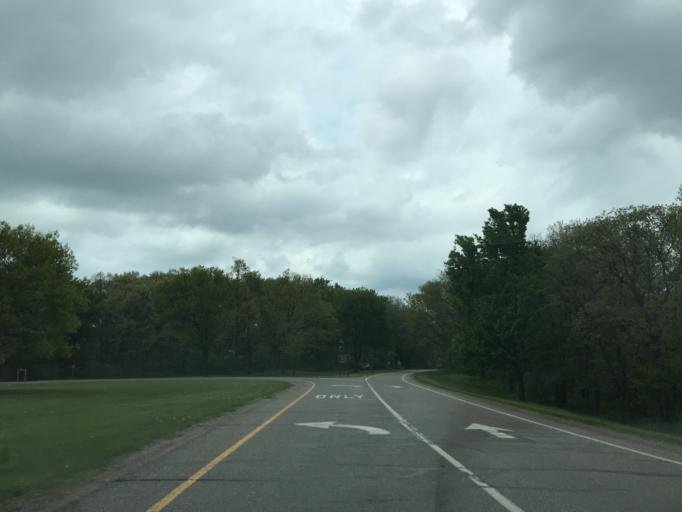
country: US
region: Michigan
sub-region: Oakland County
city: Milford
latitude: 42.5479
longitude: -83.6280
